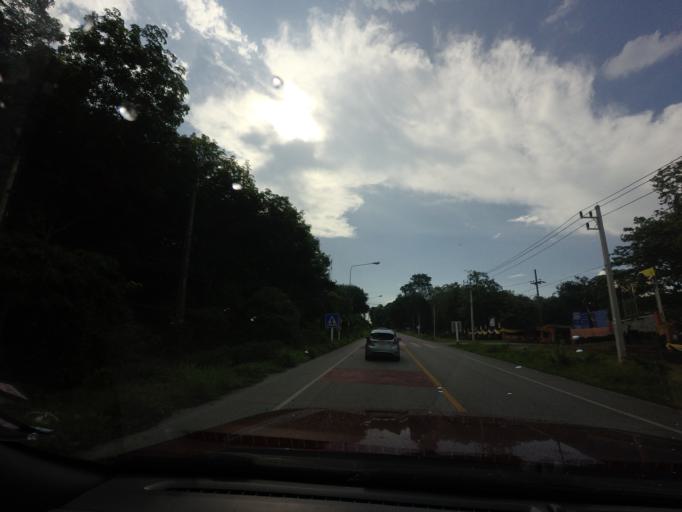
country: TH
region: Pattani
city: Mae Lan
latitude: 6.6663
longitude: 101.1630
